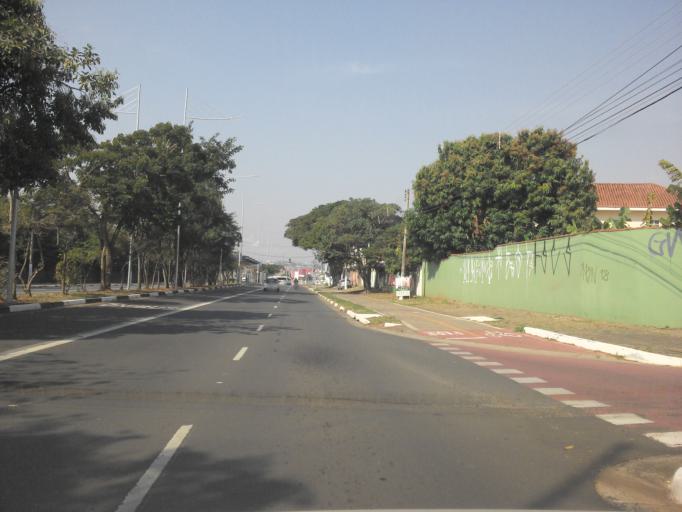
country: BR
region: Sao Paulo
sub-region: Hortolandia
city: Hortolandia
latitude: -22.8770
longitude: -47.2013
